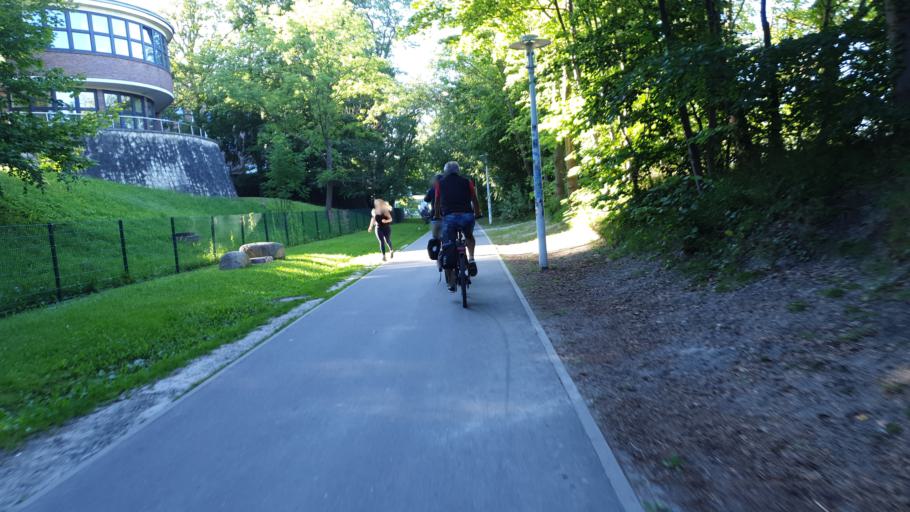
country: DE
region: Mecklenburg-Vorpommern
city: Stralsund
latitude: 54.3286
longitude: 13.0833
